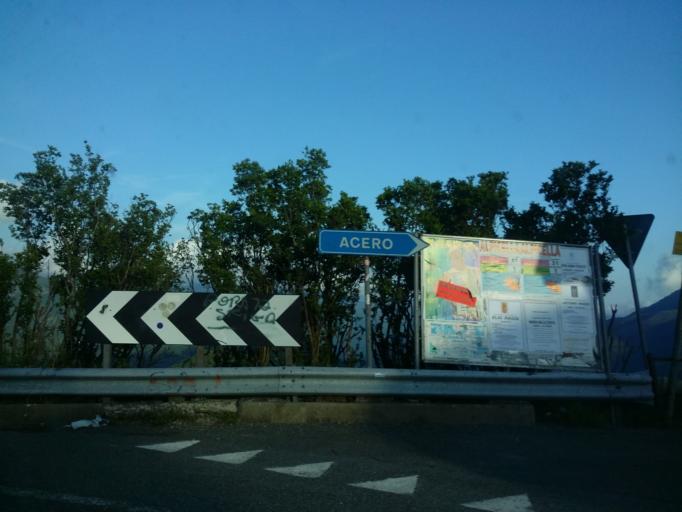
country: IT
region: Liguria
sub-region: Provincia di Genova
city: Lorsica
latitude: 44.4626
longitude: 9.3357
